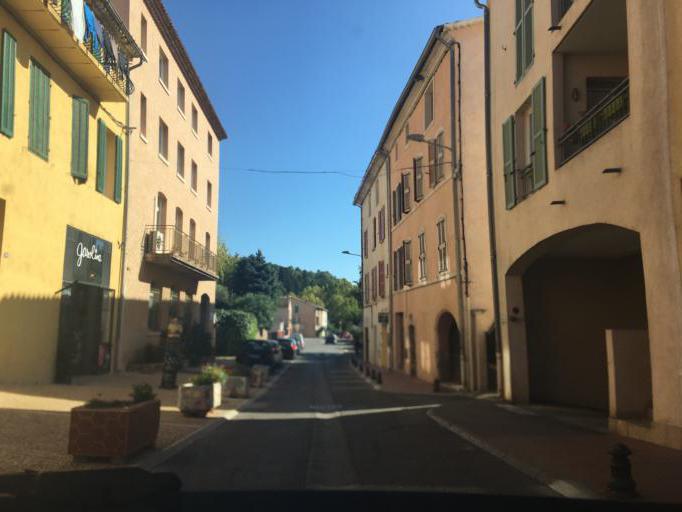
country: FR
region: Provence-Alpes-Cote d'Azur
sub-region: Departement du Var
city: Salernes
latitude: 43.5625
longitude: 6.2328
